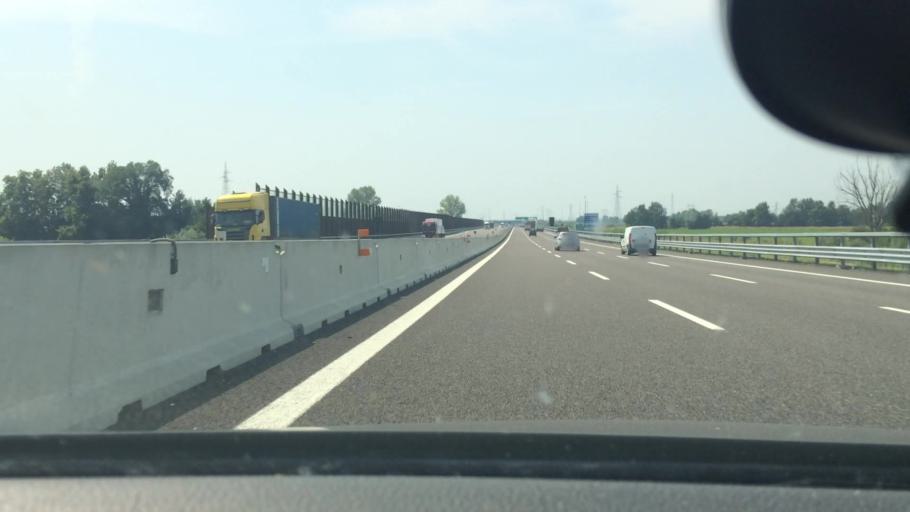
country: IT
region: Lombardy
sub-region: Provincia di Lodi
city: Merlino
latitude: 45.4405
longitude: 9.4256
